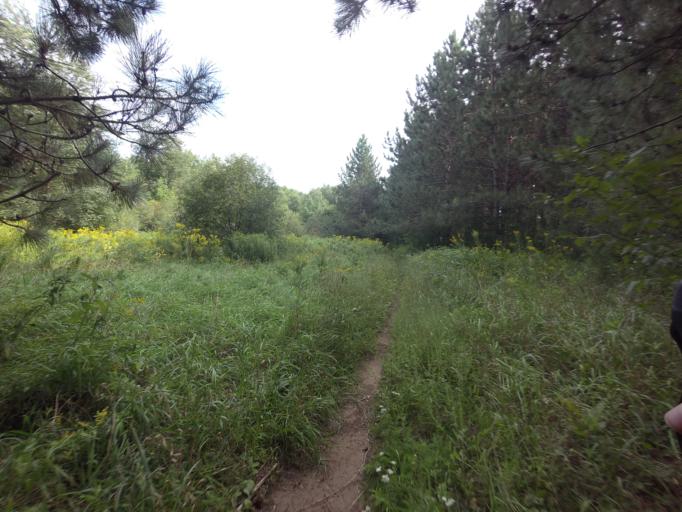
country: CA
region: Ontario
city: Bells Corners
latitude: 45.3215
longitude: -75.7994
